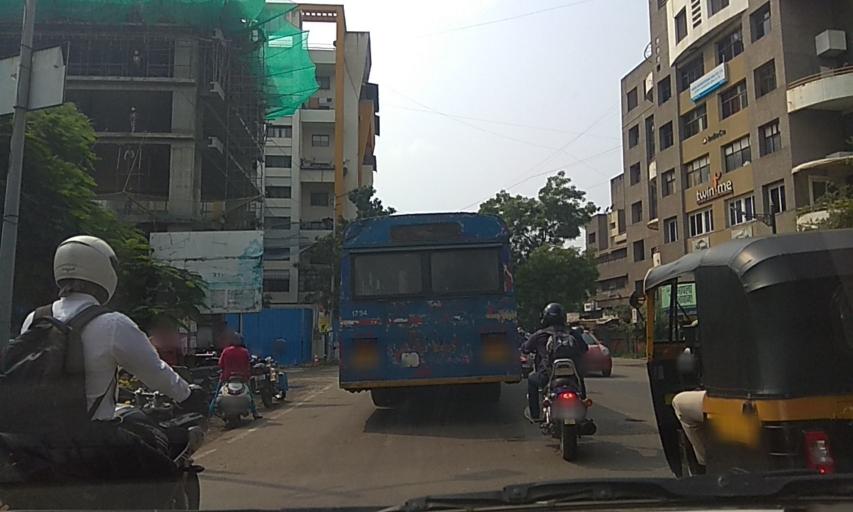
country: IN
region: Maharashtra
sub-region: Pune Division
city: Shivaji Nagar
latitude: 18.5445
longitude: 73.8388
